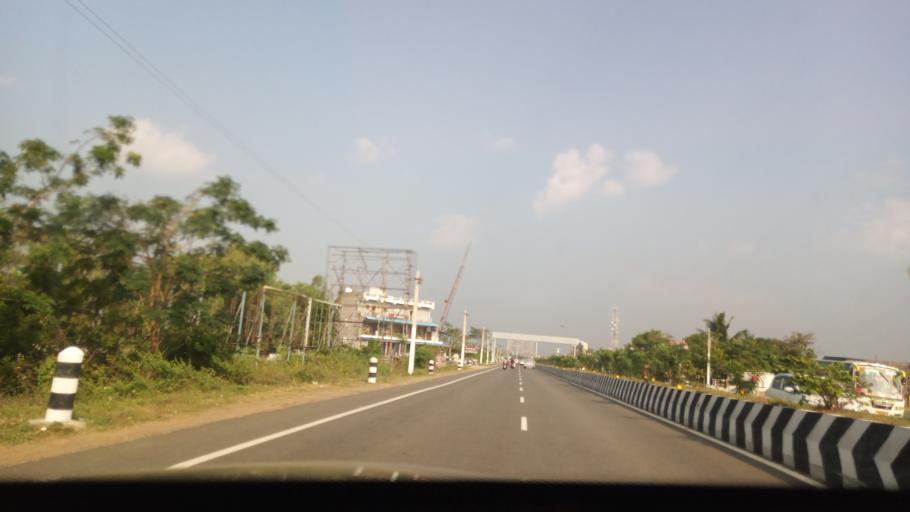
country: IN
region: Tamil Nadu
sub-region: Kancheepuram
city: Injambakkam
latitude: 12.7806
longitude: 80.2472
